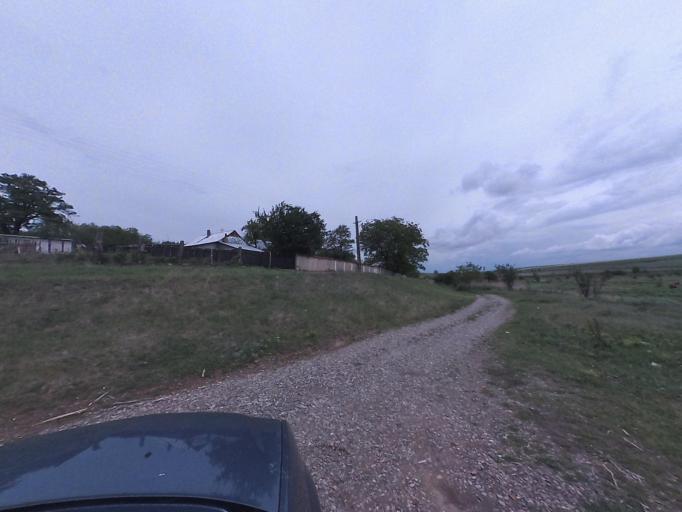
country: RO
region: Neamt
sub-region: Comuna Trifesti
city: Miron Costin
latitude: 46.9532
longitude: 26.8000
